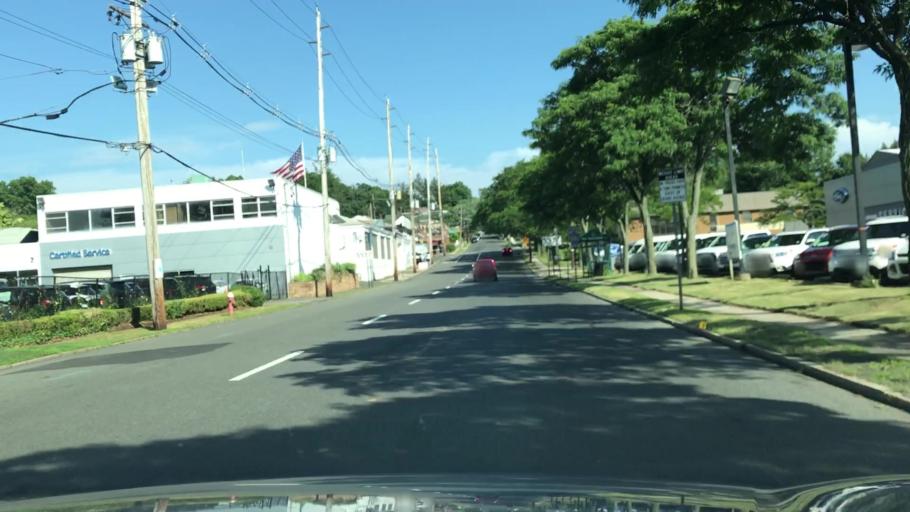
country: US
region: New Jersey
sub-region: Bergen County
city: Englewood
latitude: 40.8808
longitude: -73.9817
